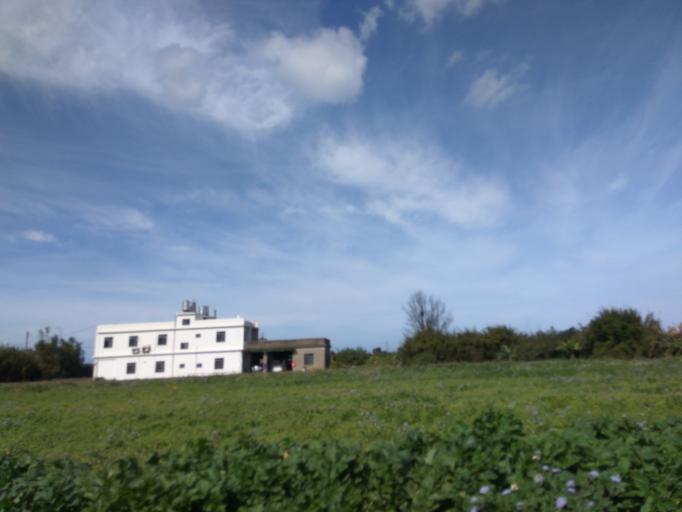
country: TW
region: Taiwan
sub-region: Hsinchu
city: Zhubei
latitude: 25.0140
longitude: 121.0755
